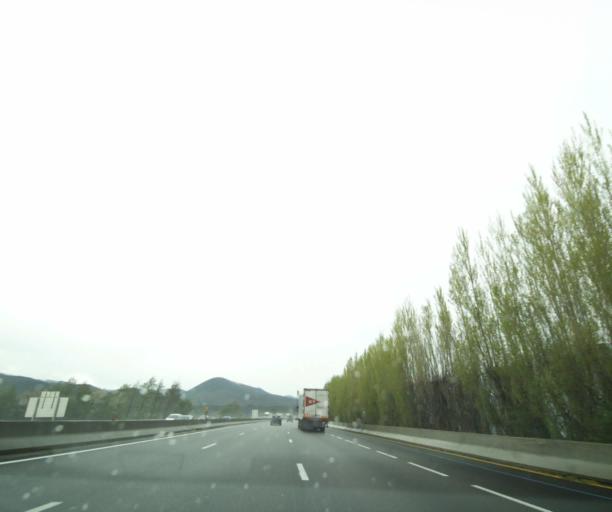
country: FR
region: Rhone-Alpes
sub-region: Departement de la Drome
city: Saulce-sur-Rhone
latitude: 44.6804
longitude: 4.7972
